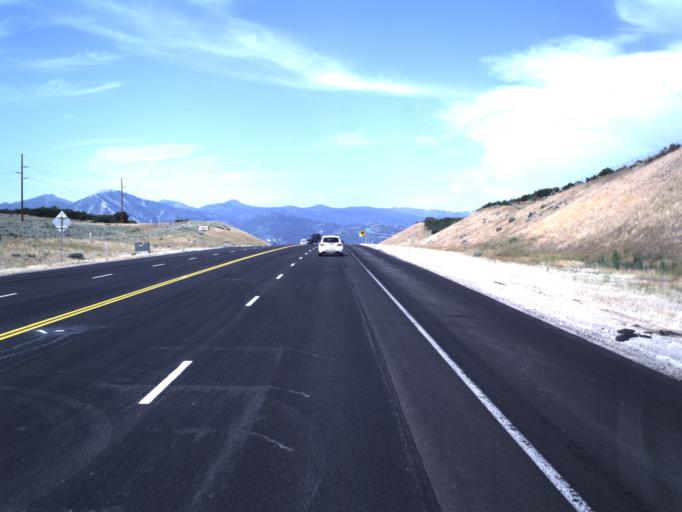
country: US
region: Utah
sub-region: Summit County
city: Kamas
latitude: 40.6343
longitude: -111.3713
